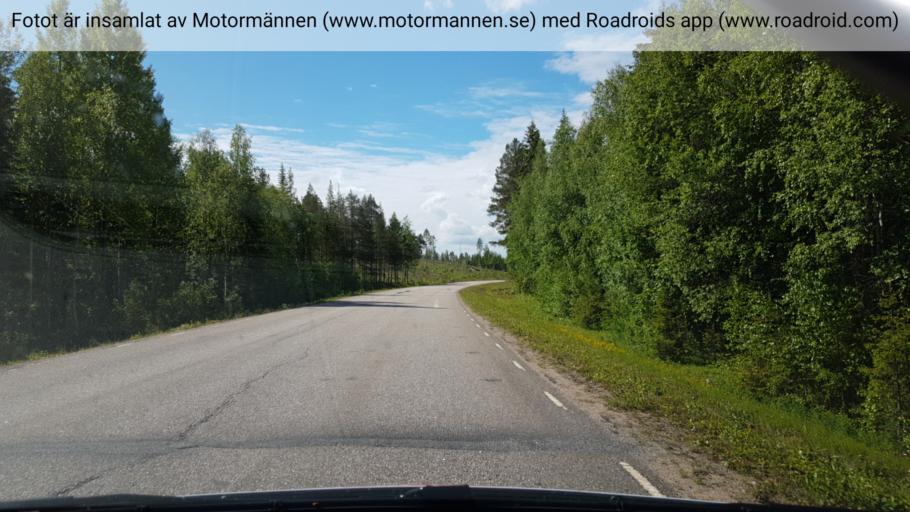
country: FI
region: Lapland
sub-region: Torniolaakso
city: Pello
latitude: 66.7215
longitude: 23.8658
